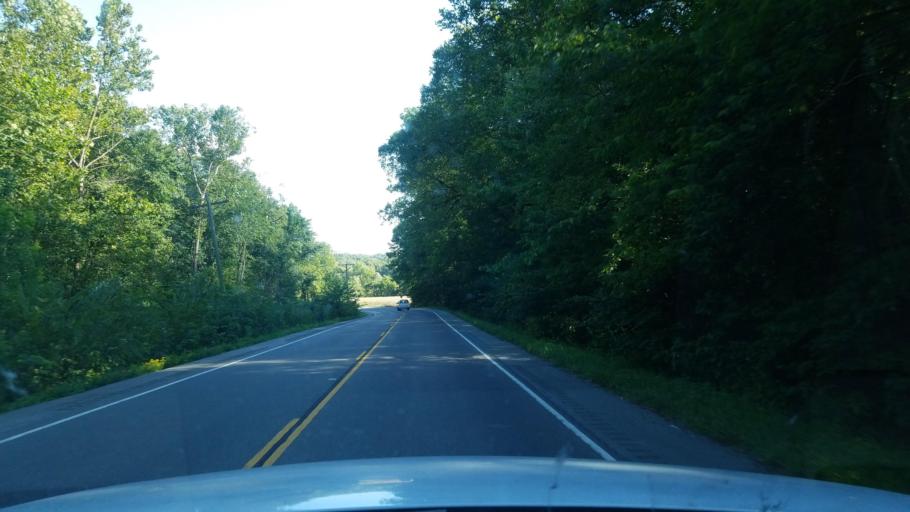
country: US
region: Illinois
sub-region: Saline County
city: Harrisburg
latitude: 37.5978
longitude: -88.4576
